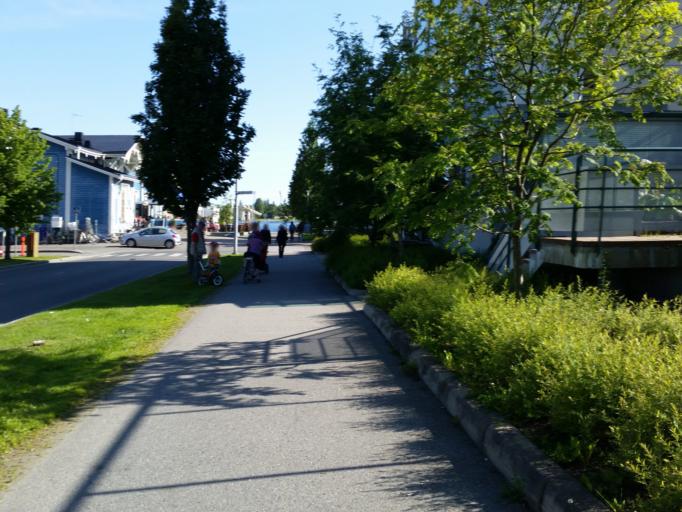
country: FI
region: Northern Savo
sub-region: Kuopio
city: Kuopio
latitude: 62.8930
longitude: 27.6962
